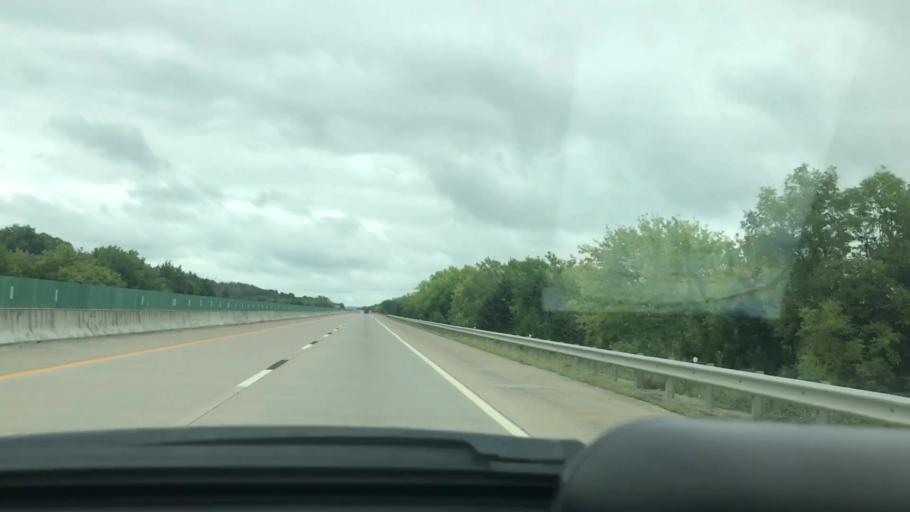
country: US
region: Oklahoma
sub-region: Pittsburg County
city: Krebs
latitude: 35.0217
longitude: -95.7166
